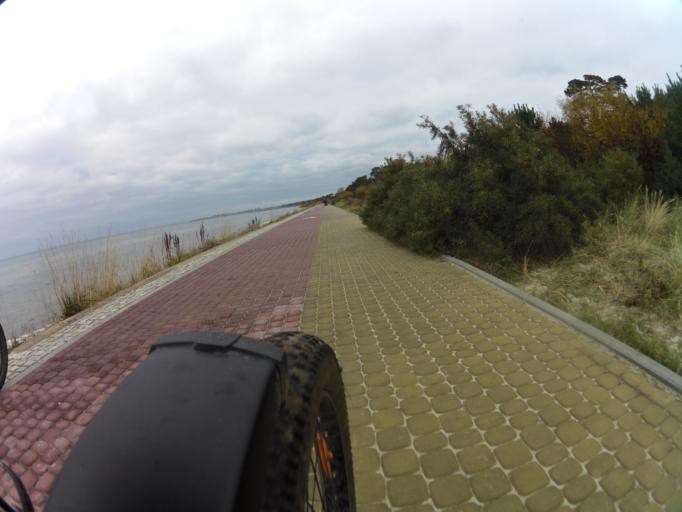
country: PL
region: Pomeranian Voivodeship
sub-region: Powiat pucki
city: Jastarnia
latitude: 54.6763
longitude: 18.7183
